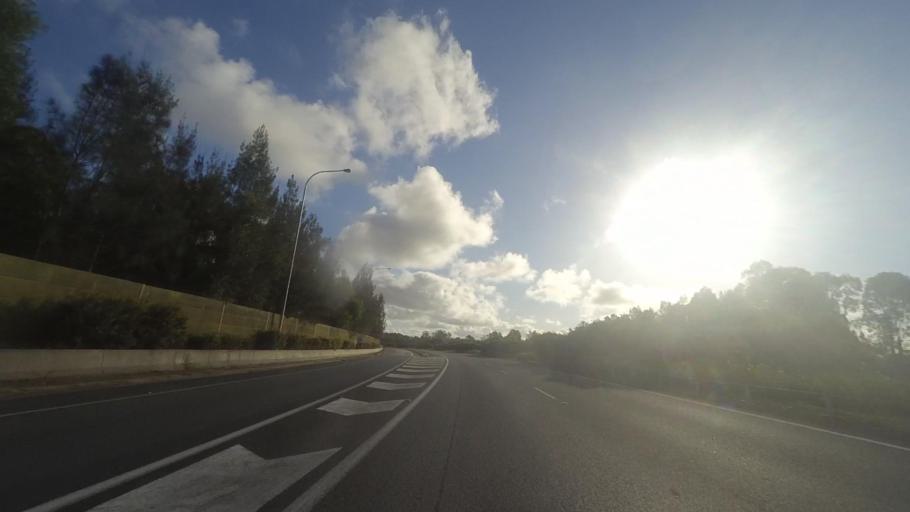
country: AU
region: New South Wales
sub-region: Great Lakes
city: Nabiac
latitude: -32.0968
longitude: 152.3777
